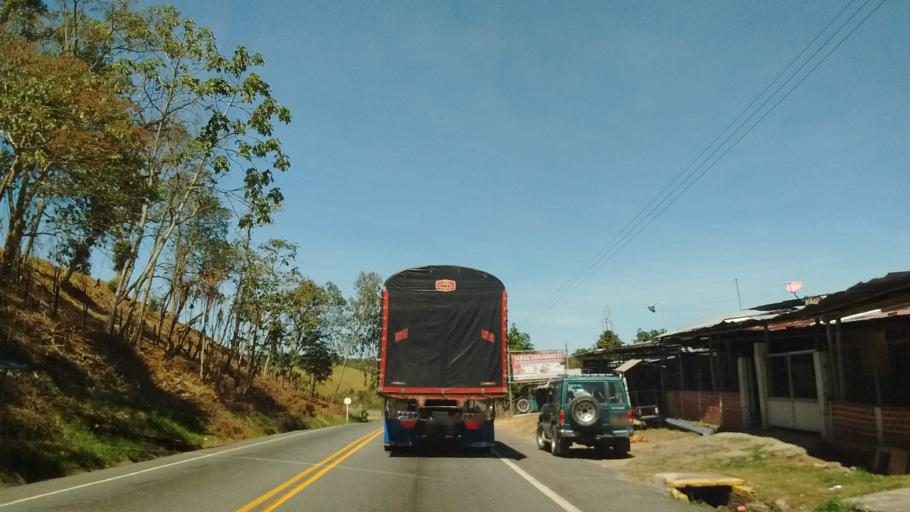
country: CO
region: Cauca
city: Popayan
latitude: 2.3832
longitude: -76.6700
